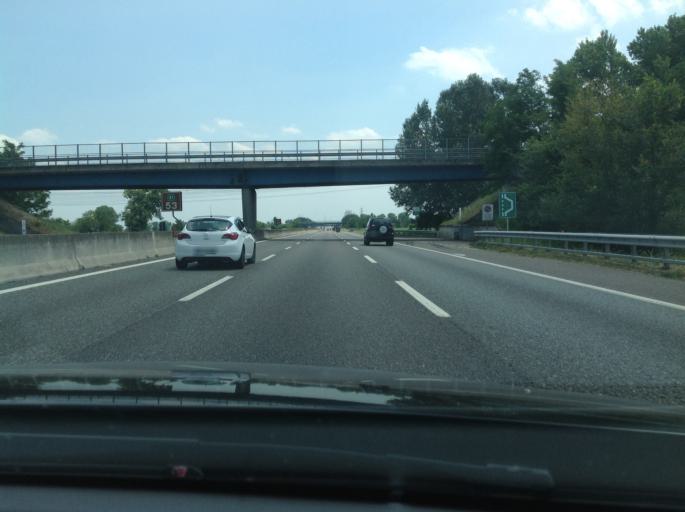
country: IT
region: Lombardy
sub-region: Provincia di Lodi
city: San Rocco al Porto
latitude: 45.0967
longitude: 9.7020
